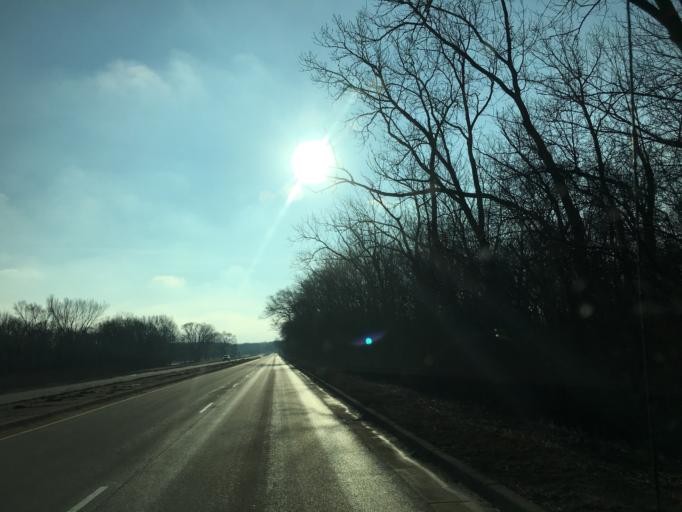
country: US
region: Illinois
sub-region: Cook County
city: Rolling Meadows
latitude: 42.0334
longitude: -88.0183
